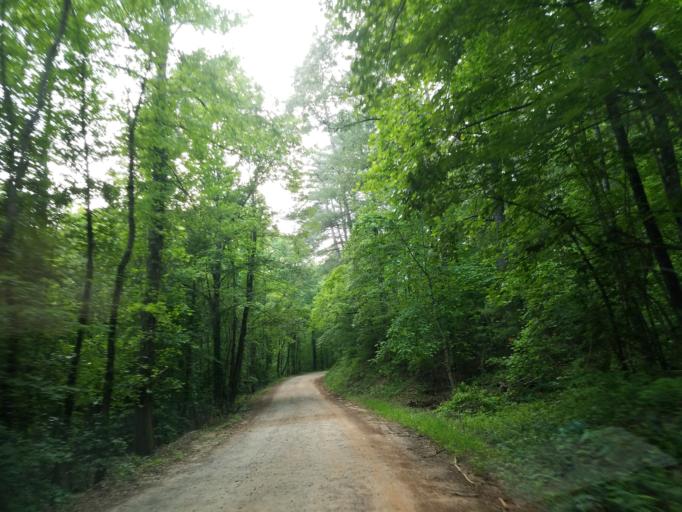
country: US
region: Georgia
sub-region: Lumpkin County
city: Dahlonega
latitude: 34.6037
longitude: -84.1033
